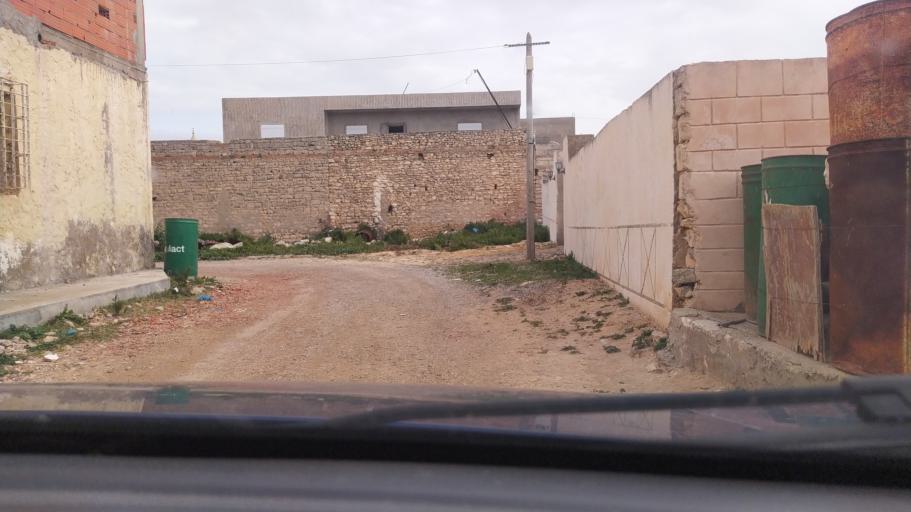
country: TN
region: Al Munastir
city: Sidi Bin Nur
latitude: 35.5169
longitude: 10.9244
